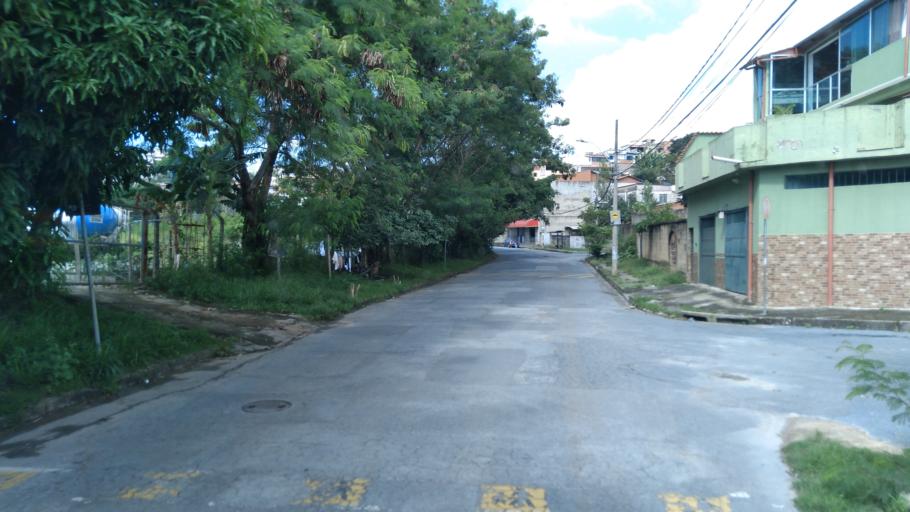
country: BR
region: Minas Gerais
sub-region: Santa Luzia
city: Santa Luzia
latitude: -19.8249
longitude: -43.8976
